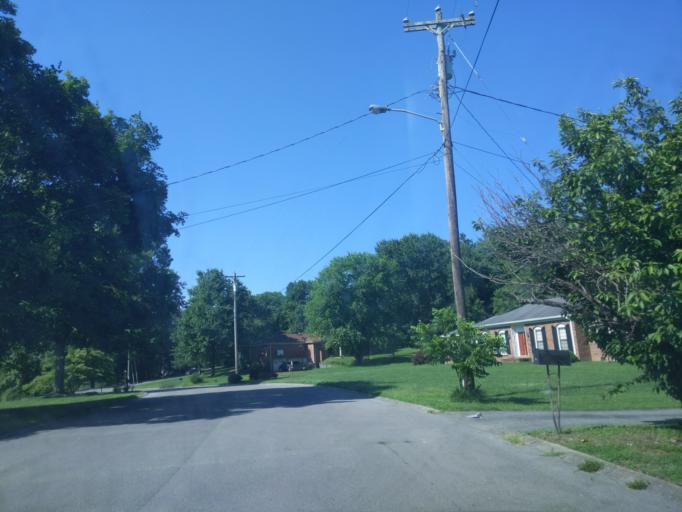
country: US
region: Tennessee
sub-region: Williamson County
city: Brentwood Estates
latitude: 36.0330
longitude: -86.7601
